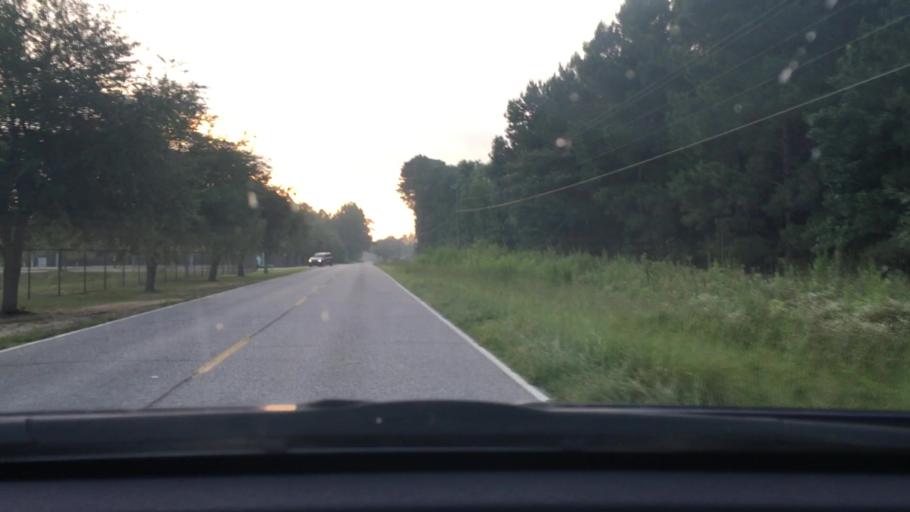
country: US
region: South Carolina
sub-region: Darlington County
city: Hartsville
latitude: 34.3509
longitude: -80.0878
